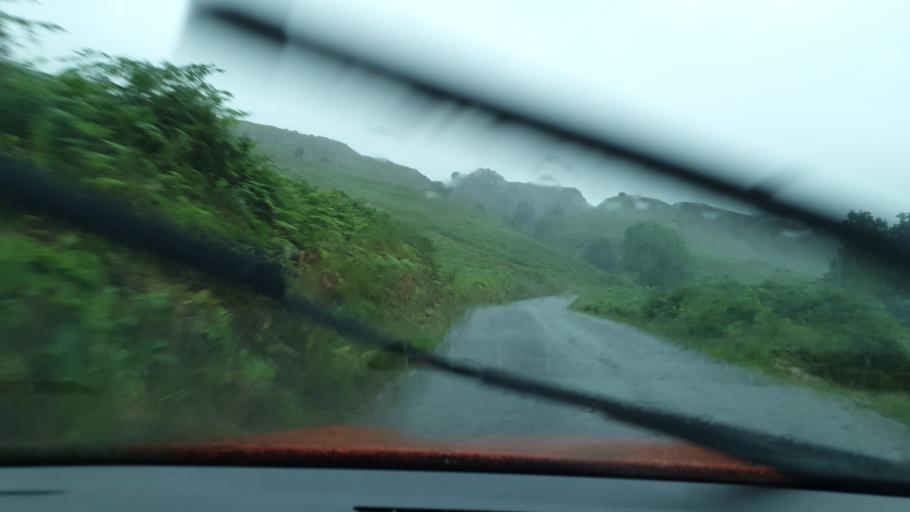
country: GB
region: England
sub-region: Cumbria
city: Millom
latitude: 54.3125
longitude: -3.2293
